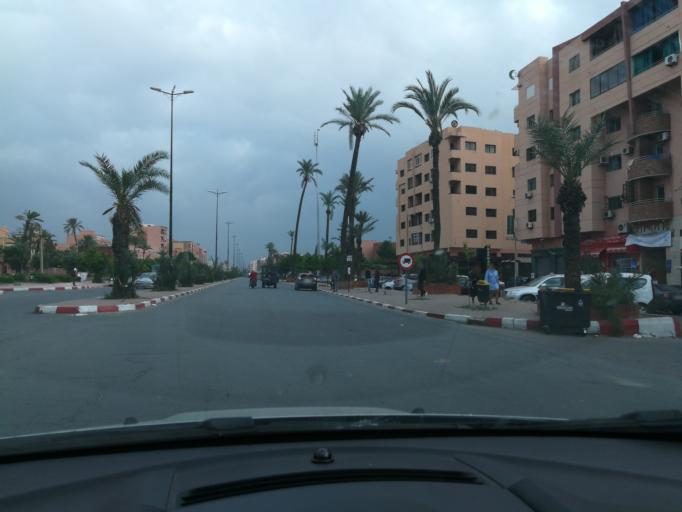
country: MA
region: Marrakech-Tensift-Al Haouz
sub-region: Marrakech
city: Marrakesh
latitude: 31.6523
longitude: -8.0170
